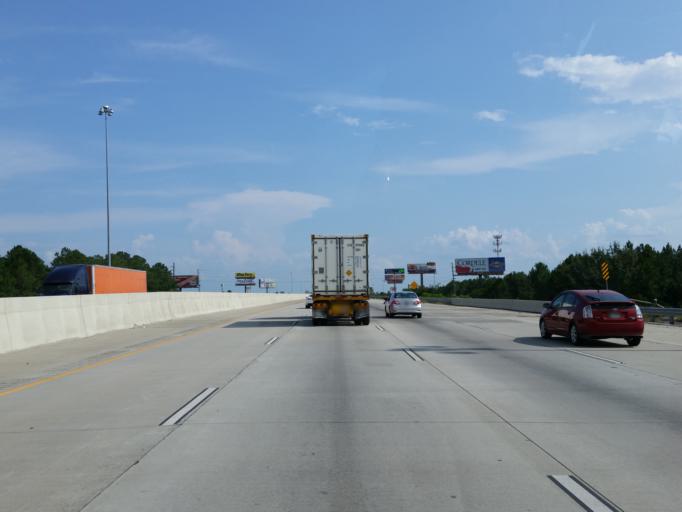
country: US
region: Georgia
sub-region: Crisp County
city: Cordele
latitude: 31.9689
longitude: -83.7531
